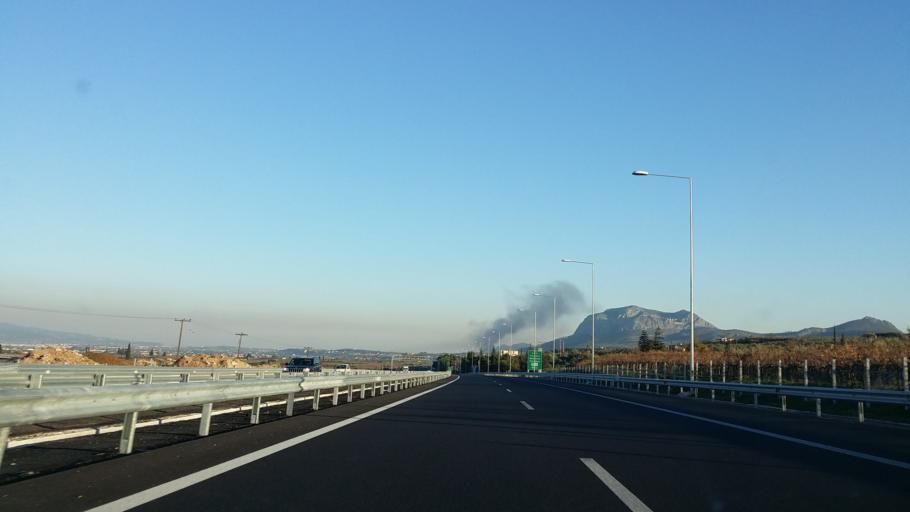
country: GR
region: Peloponnese
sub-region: Nomos Korinthias
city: Zevgolateio
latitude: 37.9231
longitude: 22.8056
